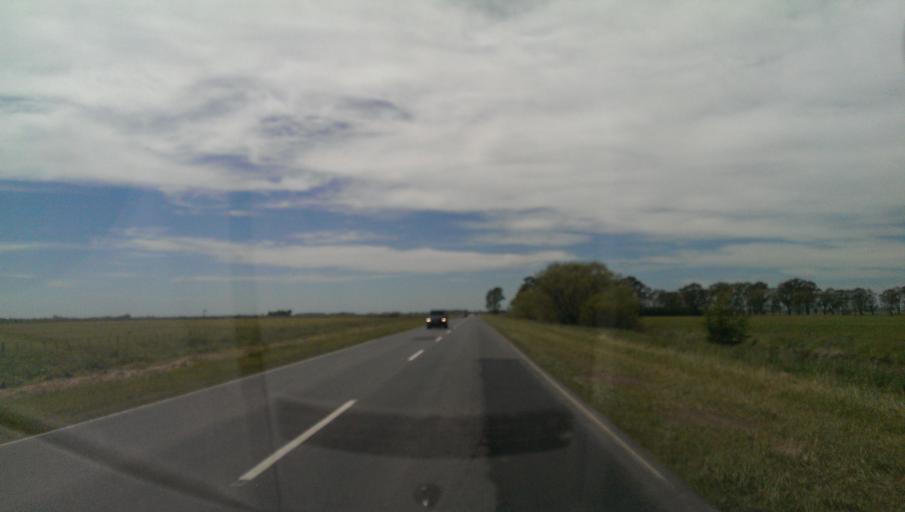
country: AR
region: Buenos Aires
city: Olavarria
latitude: -37.0200
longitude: -60.4117
